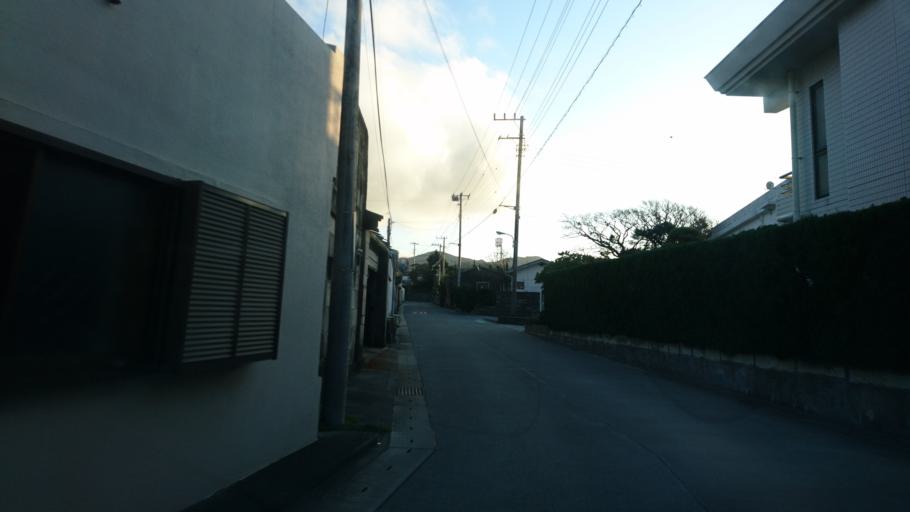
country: JP
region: Shizuoka
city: Shimoda
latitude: 34.3764
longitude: 139.2575
